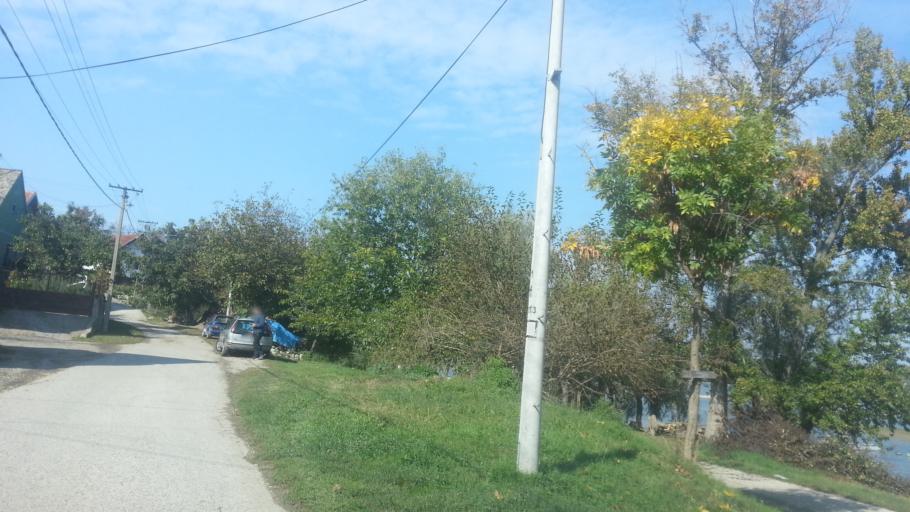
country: RS
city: Novi Slankamen
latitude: 45.1506
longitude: 20.2474
